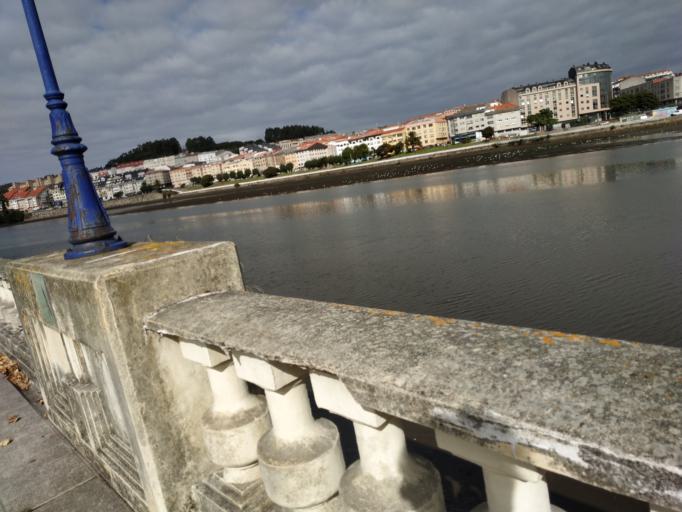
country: ES
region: Galicia
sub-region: Provincia da Coruna
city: Cambre
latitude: 43.3161
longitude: -8.3607
